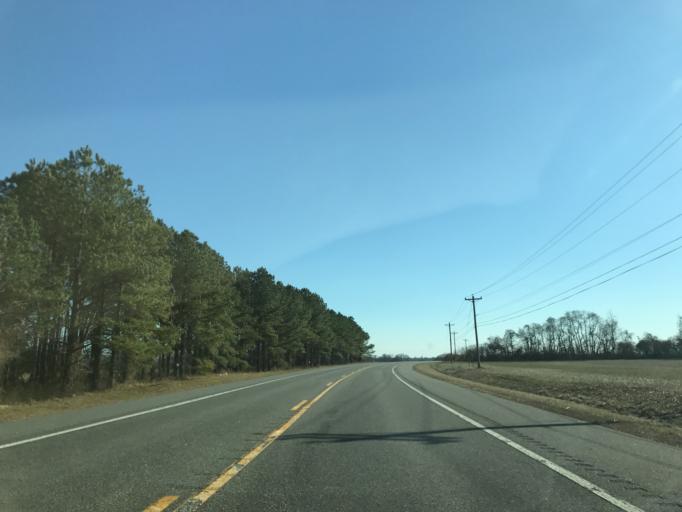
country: US
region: Maryland
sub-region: Queen Anne's County
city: Centreville
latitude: 38.9793
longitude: -76.0702
